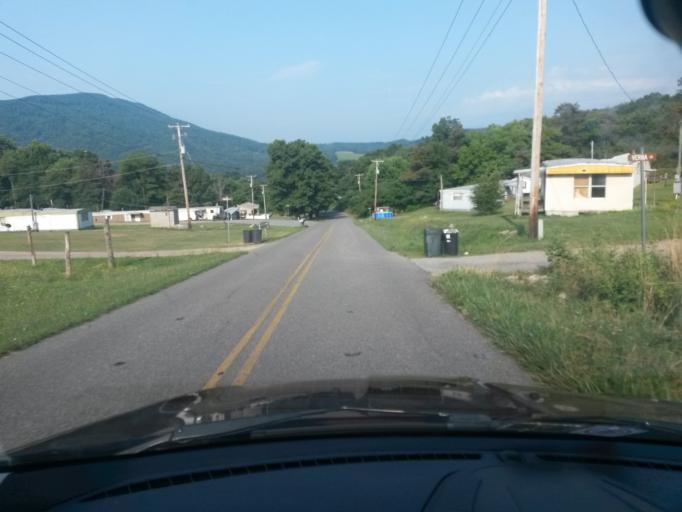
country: US
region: Virginia
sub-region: Giles County
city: Narrows
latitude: 37.3706
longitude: -80.8036
